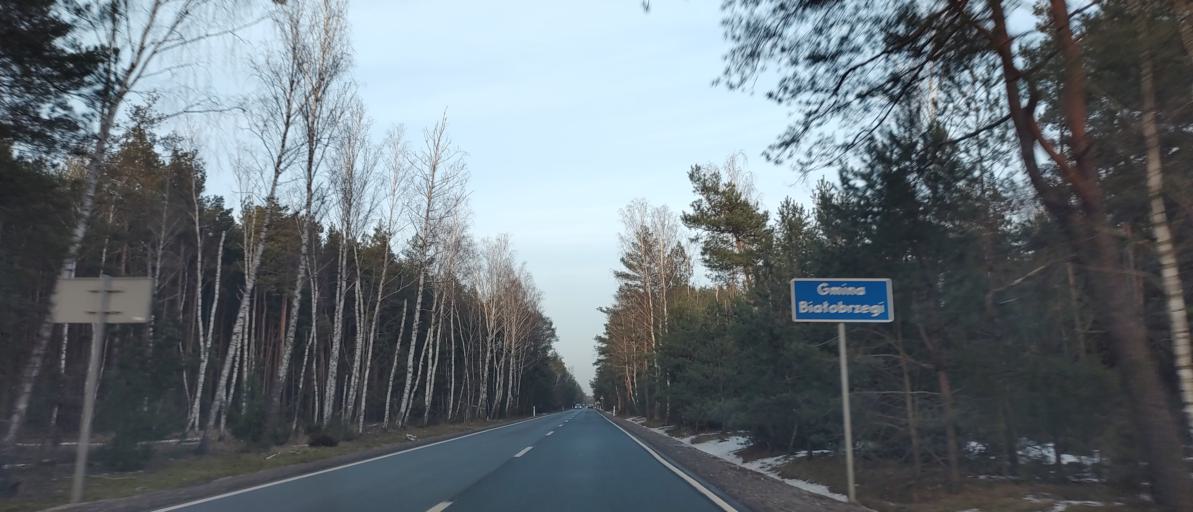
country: PL
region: Masovian Voivodeship
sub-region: Powiat bialobrzeski
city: Bialobrzegi
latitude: 51.6386
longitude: 20.9099
